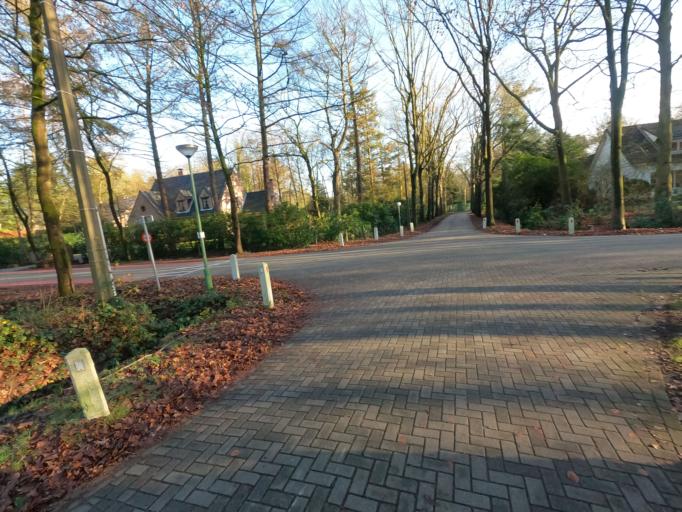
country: BE
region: Flanders
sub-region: Provincie Antwerpen
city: Schilde
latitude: 51.2775
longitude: 4.6154
